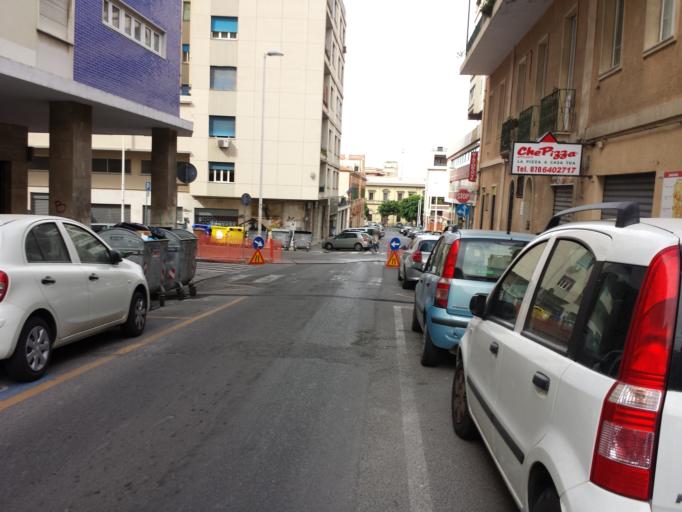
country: IT
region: Sardinia
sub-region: Provincia di Cagliari
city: Cagliari
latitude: 39.2191
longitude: 9.1087
